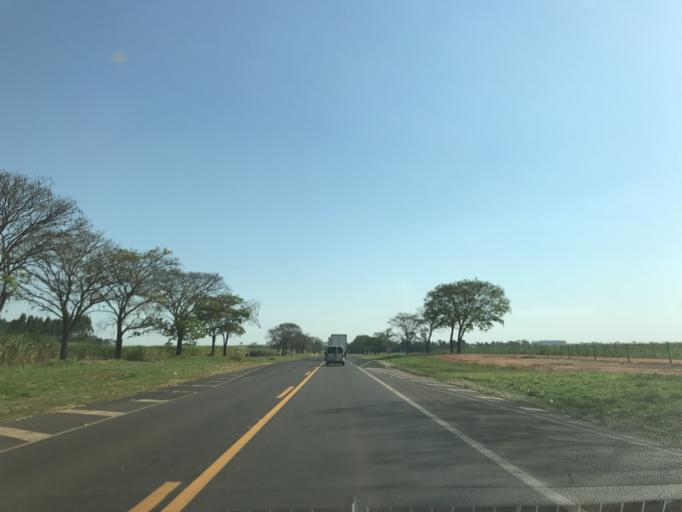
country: BR
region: Sao Paulo
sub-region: Penapolis
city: Penapolis
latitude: -21.4747
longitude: -50.1946
